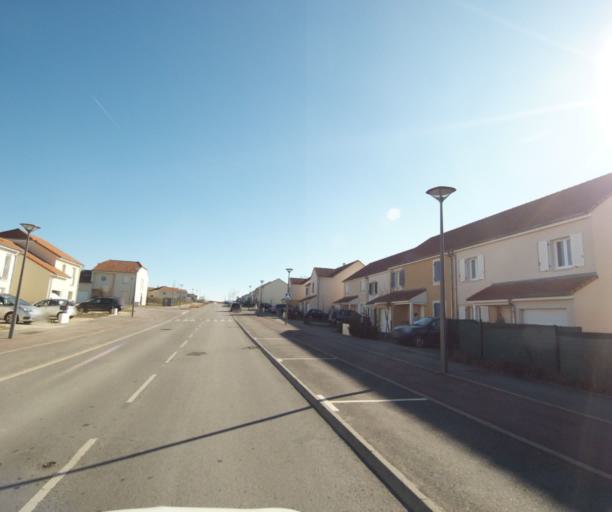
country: FR
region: Lorraine
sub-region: Departement de Meurthe-et-Moselle
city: Tomblaine
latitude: 48.6794
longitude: 6.2269
